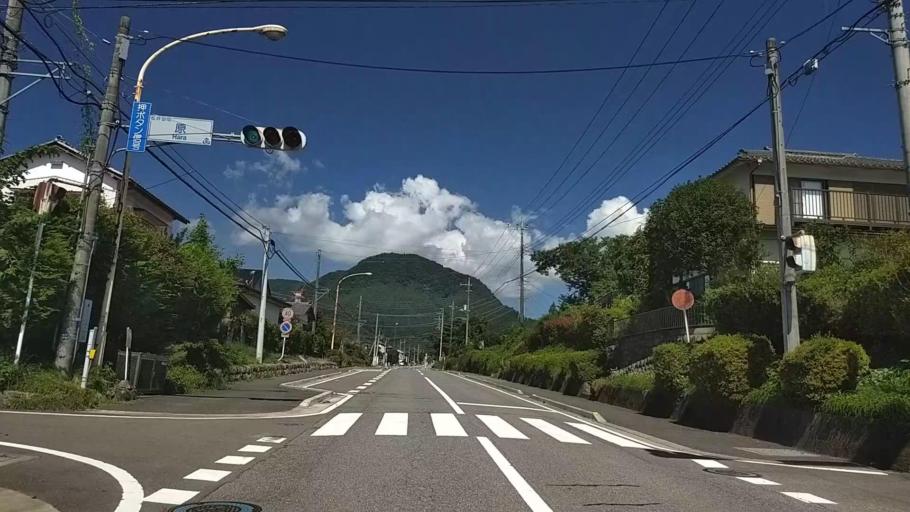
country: JP
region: Gunma
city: Annaka
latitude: 36.3455
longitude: 138.7221
